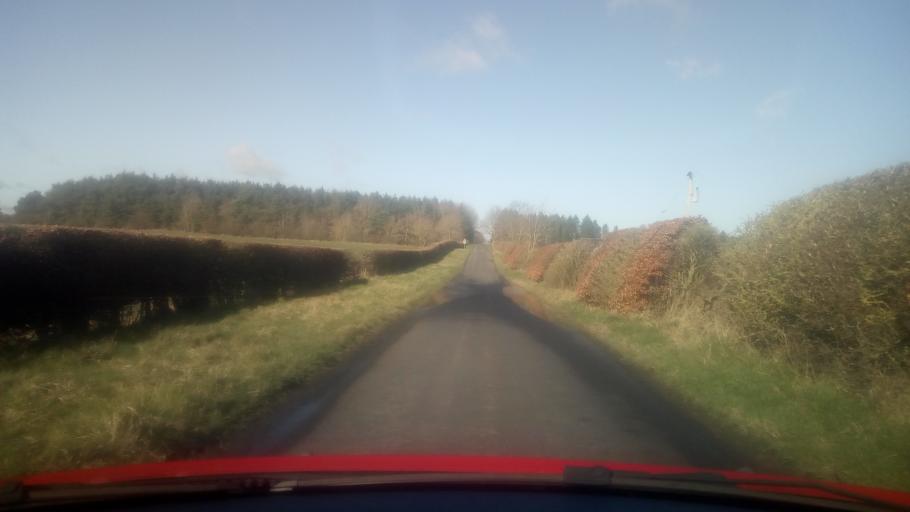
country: GB
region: Scotland
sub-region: The Scottish Borders
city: Saint Boswells
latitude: 55.5349
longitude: -2.6506
